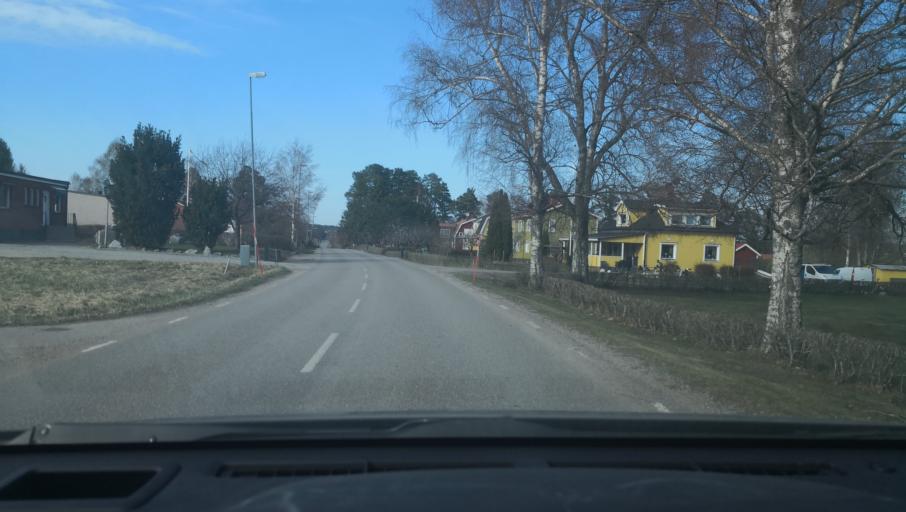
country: SE
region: Uppsala
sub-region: Heby Kommun
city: Heby
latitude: 59.9267
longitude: 16.8553
